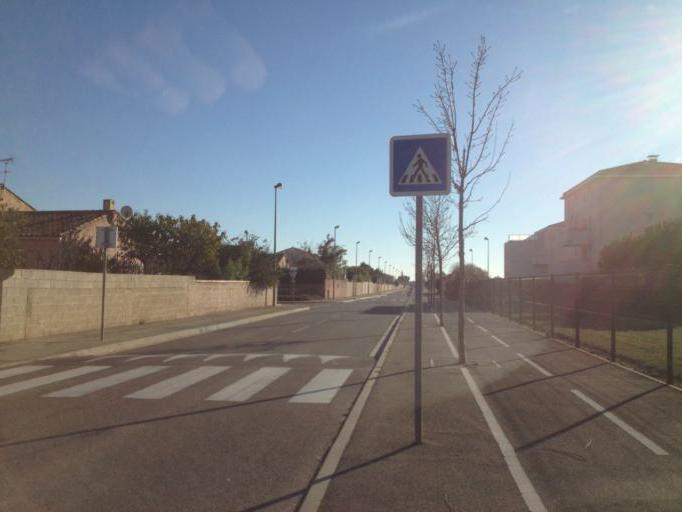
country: FR
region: Provence-Alpes-Cote d'Azur
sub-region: Departement des Bouches-du-Rhone
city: Istres
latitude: 43.5124
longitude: 4.9675
